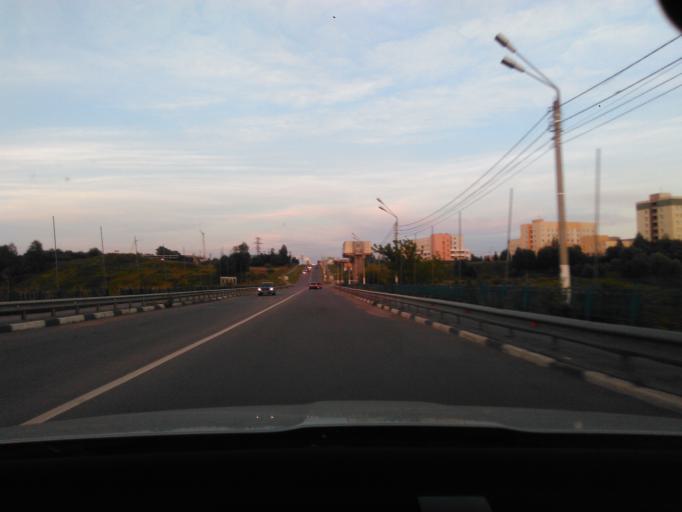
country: RU
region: Moskovskaya
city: Klin
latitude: 56.3183
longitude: 36.7347
